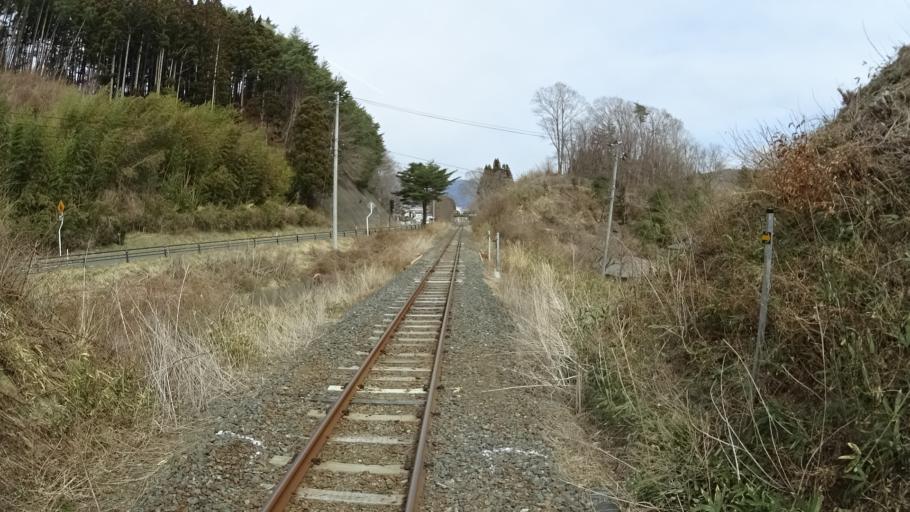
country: JP
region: Iwate
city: Yamada
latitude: 39.4267
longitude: 141.9723
